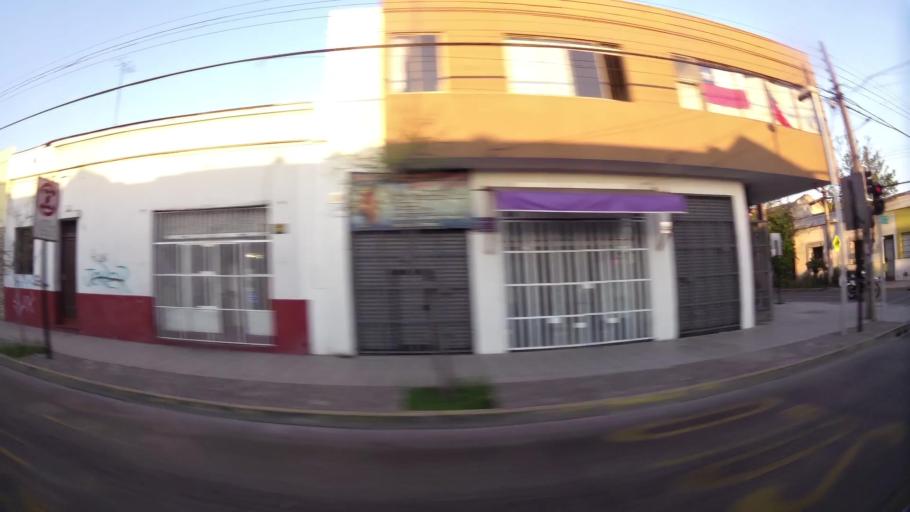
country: CL
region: Santiago Metropolitan
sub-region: Provincia de Santiago
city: Santiago
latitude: -33.4624
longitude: -70.6726
